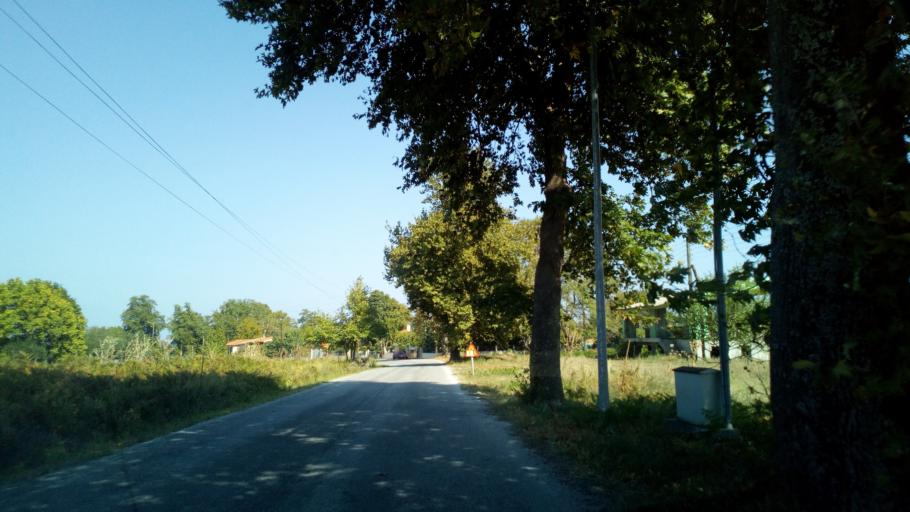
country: GR
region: Central Macedonia
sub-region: Nomos Chalkidikis
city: Stratonion
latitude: 40.5946
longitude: 23.7743
